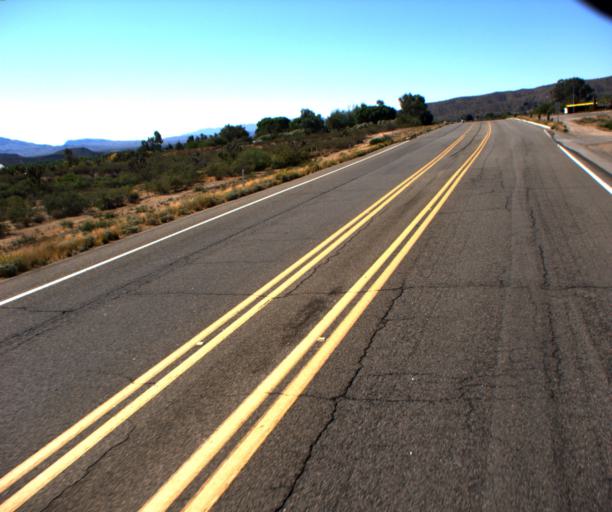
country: US
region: Arizona
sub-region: Yavapai County
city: Bagdad
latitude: 34.7148
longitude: -113.6143
